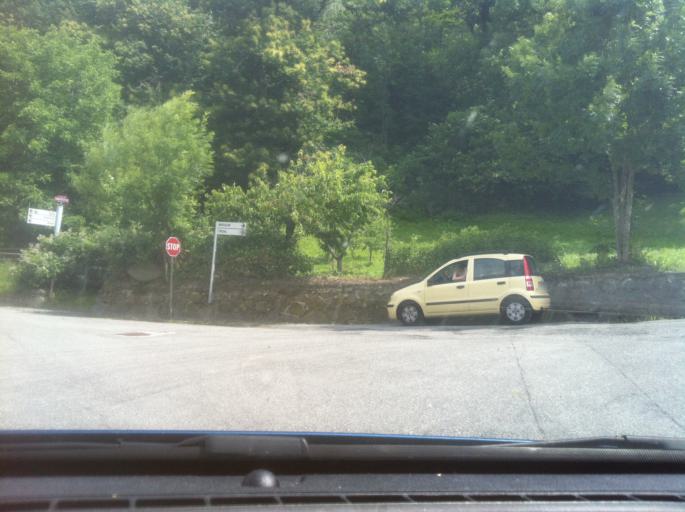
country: IT
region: Aosta Valley
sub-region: Valle d'Aosta
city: Saint Marcel
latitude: 45.7280
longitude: 7.4476
